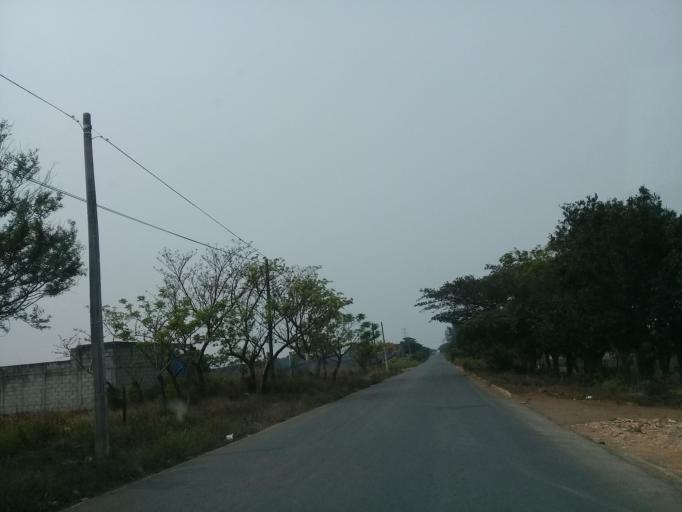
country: MX
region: Veracruz
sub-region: Medellin
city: La Laguna y Monte del Castillo
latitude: 18.9835
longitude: -96.1177
